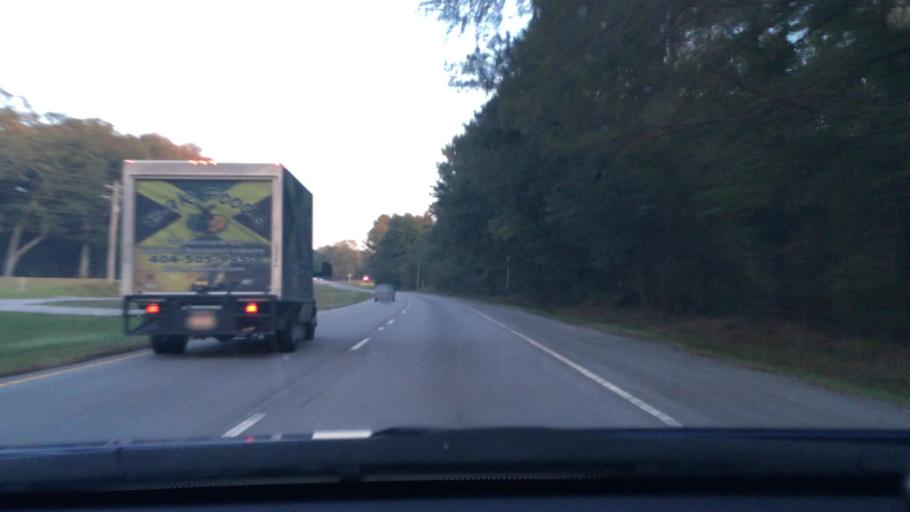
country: US
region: South Carolina
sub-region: Richland County
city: Gadsden
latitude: 33.9443
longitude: -80.7507
